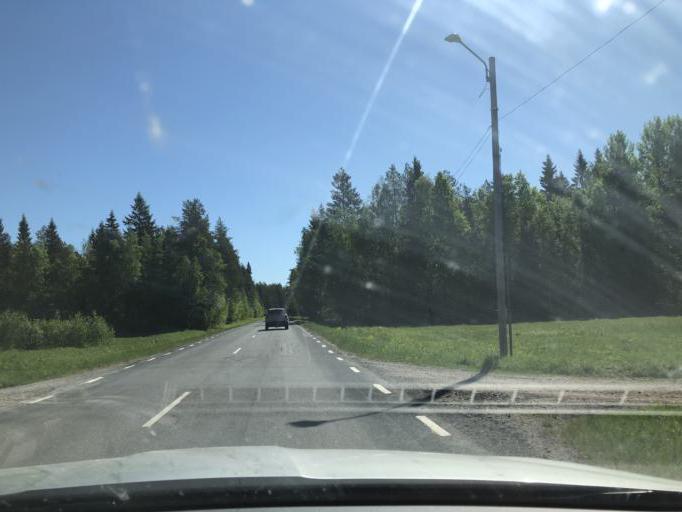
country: SE
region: Norrbotten
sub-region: Lulea Kommun
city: Gammelstad
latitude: 65.6563
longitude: 22.0048
